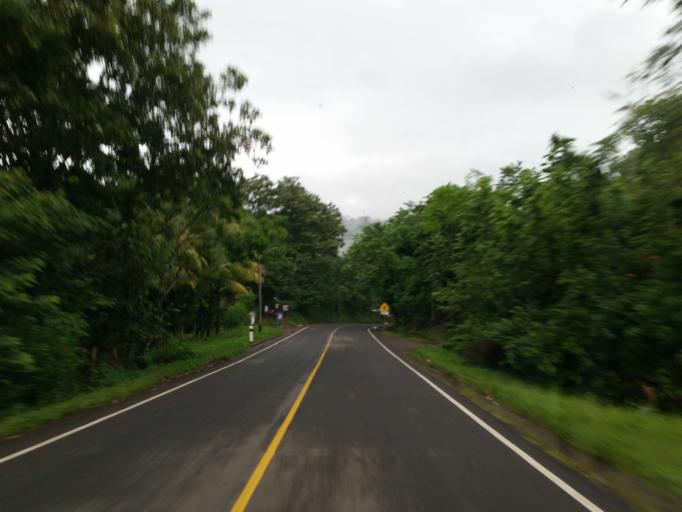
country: NI
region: Matagalpa
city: San Ramon
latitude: 13.1141
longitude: -85.7493
